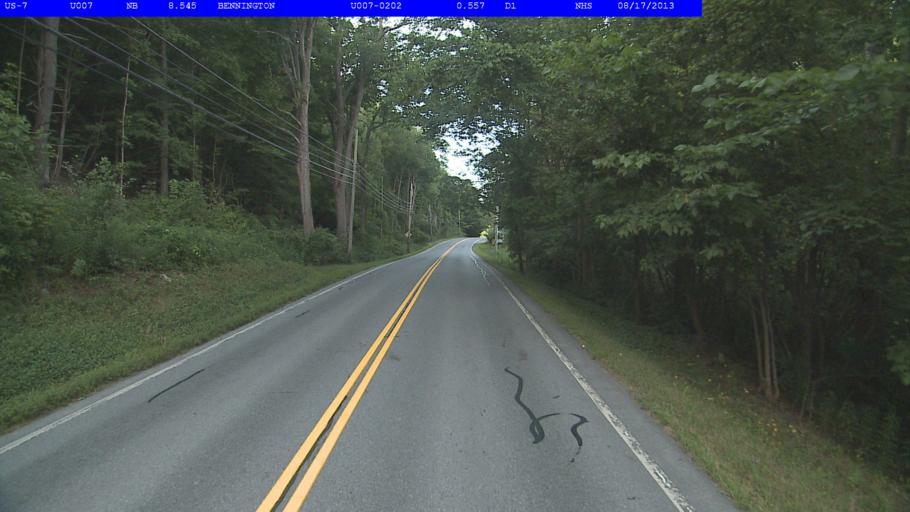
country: US
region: Vermont
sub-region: Bennington County
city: Bennington
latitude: 42.8453
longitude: -73.2018
